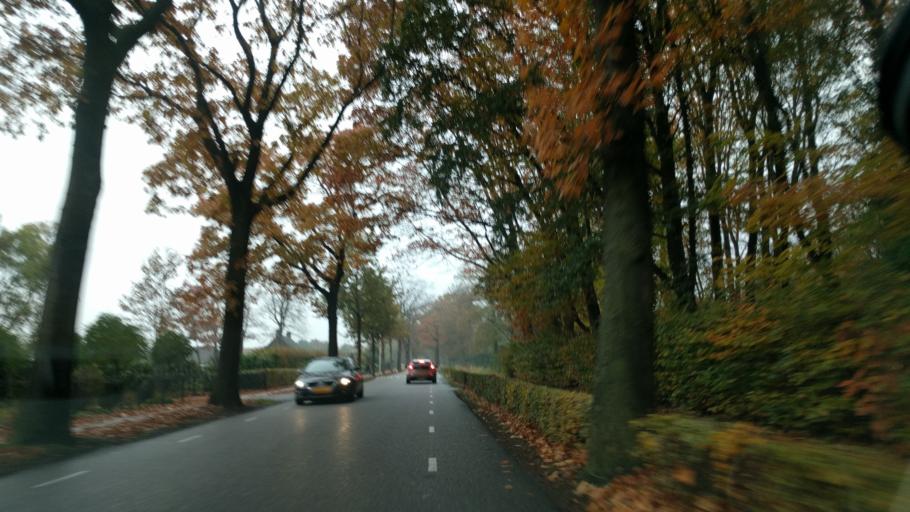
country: NL
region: North Brabant
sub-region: Gemeente Rucphen
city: Rucphen
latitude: 51.5457
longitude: 4.5467
